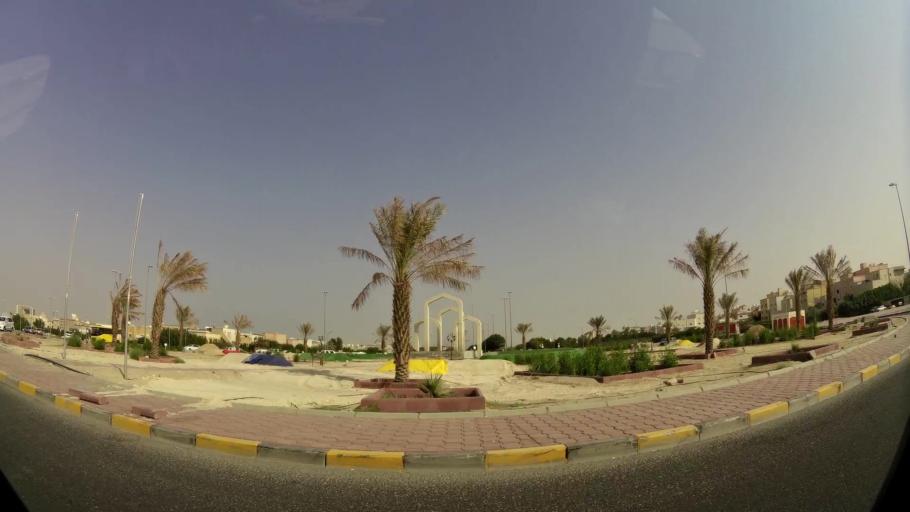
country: KW
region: Muhafazat al Jahra'
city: Al Jahra'
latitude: 29.3372
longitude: 47.6490
